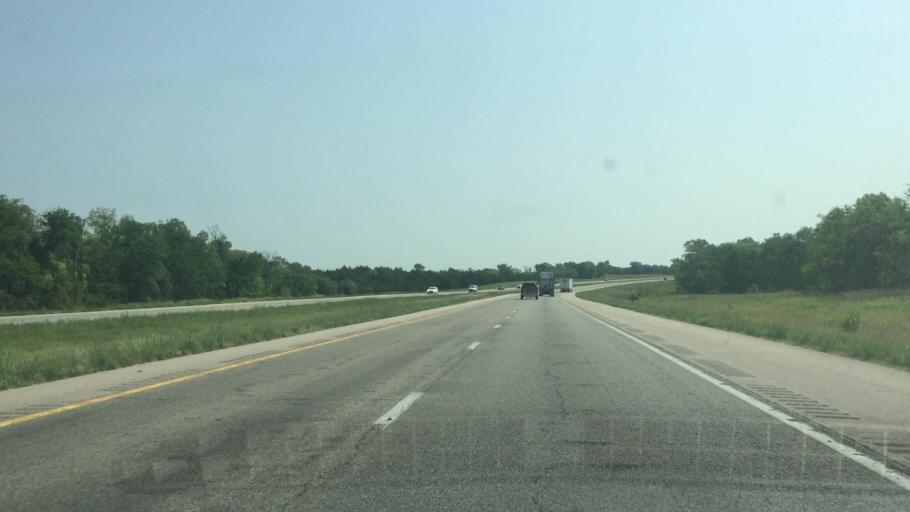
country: US
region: Kansas
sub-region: Osage County
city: Osage City
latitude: 38.4266
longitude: -95.8908
